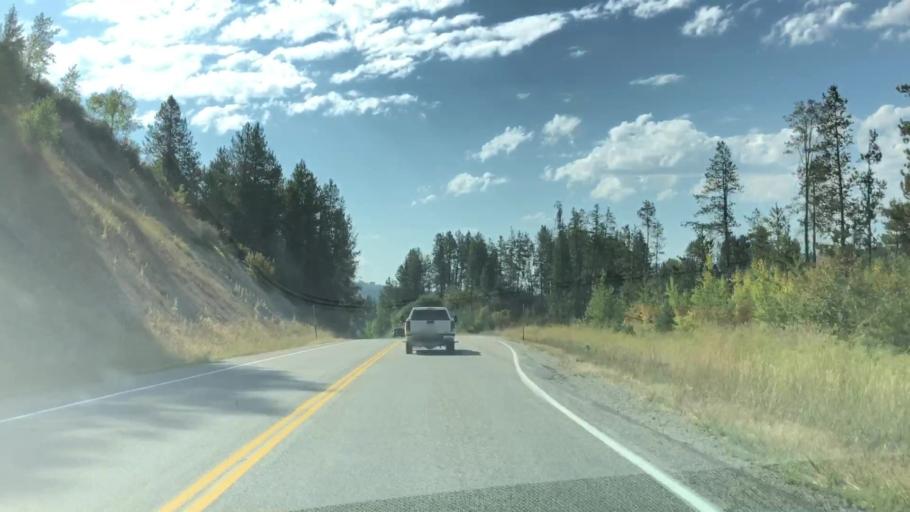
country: US
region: Idaho
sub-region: Teton County
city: Victor
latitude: 43.2874
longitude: -111.1214
